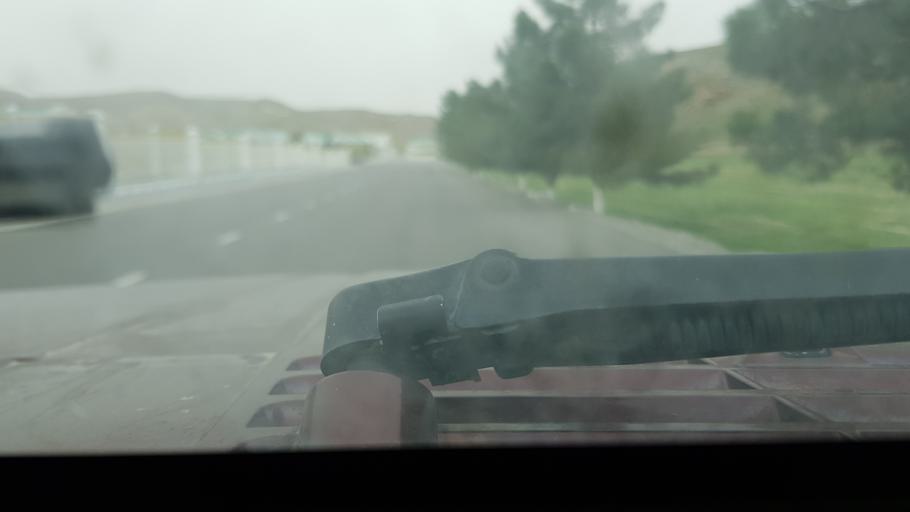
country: TM
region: Ahal
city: Arcabil
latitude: 38.0381
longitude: 58.0114
